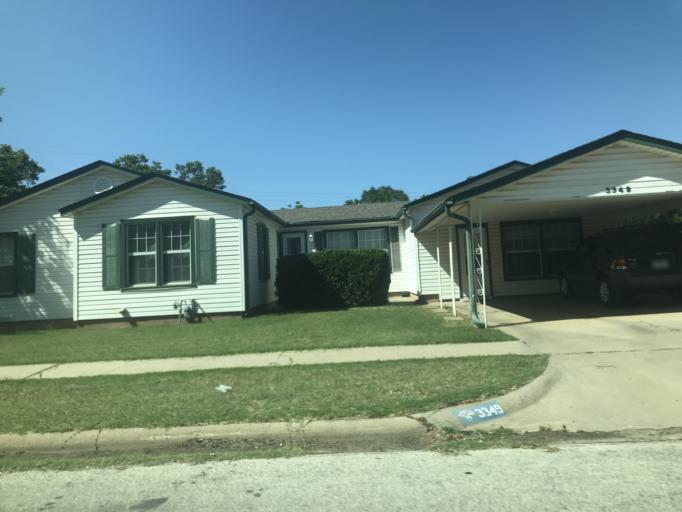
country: US
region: Texas
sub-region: Taylor County
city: Abilene
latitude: 32.4098
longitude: -99.7539
